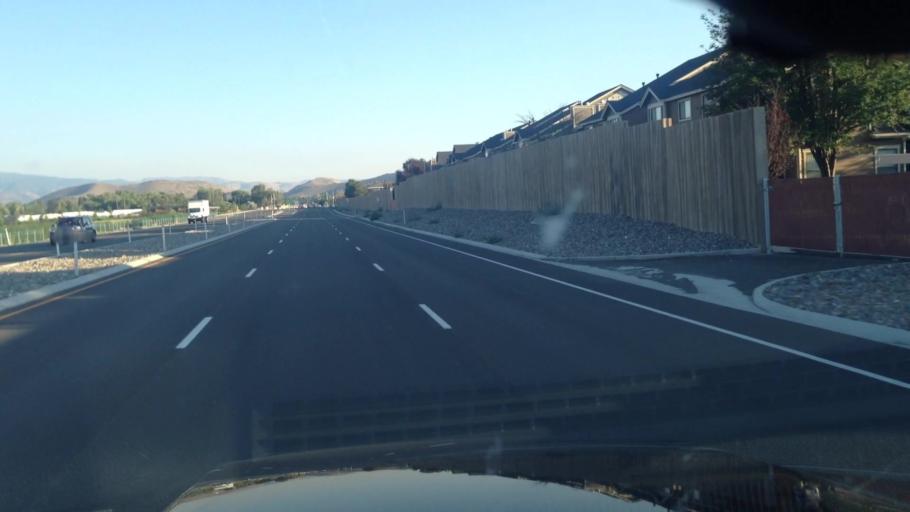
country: US
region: Nevada
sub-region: Washoe County
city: Sparks
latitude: 39.5033
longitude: -119.7482
